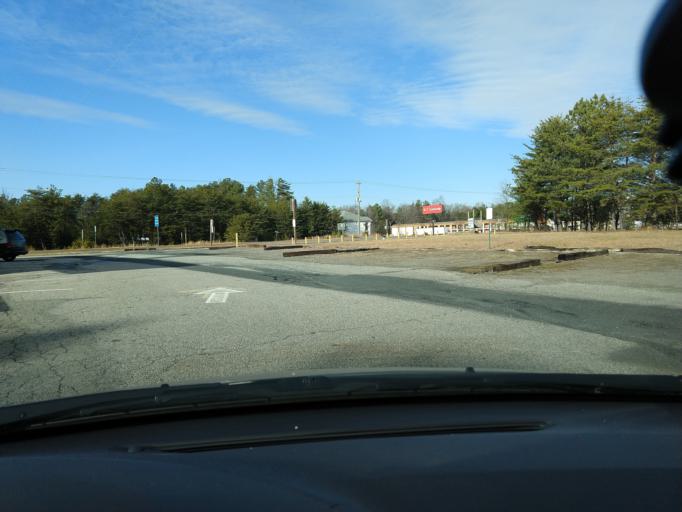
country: US
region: Virginia
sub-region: Hanover County
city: Ashland
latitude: 37.9310
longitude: -77.4788
